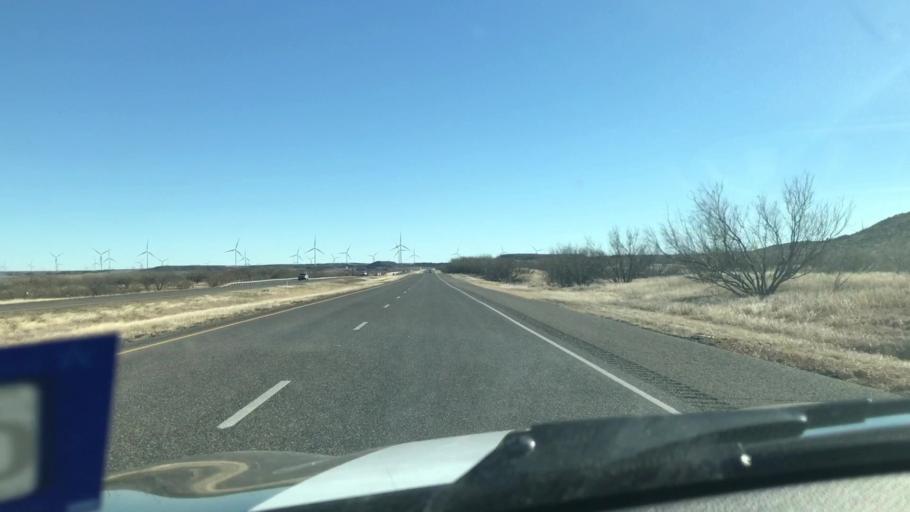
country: US
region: Texas
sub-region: Scurry County
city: Snyder
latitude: 32.9332
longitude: -101.0711
